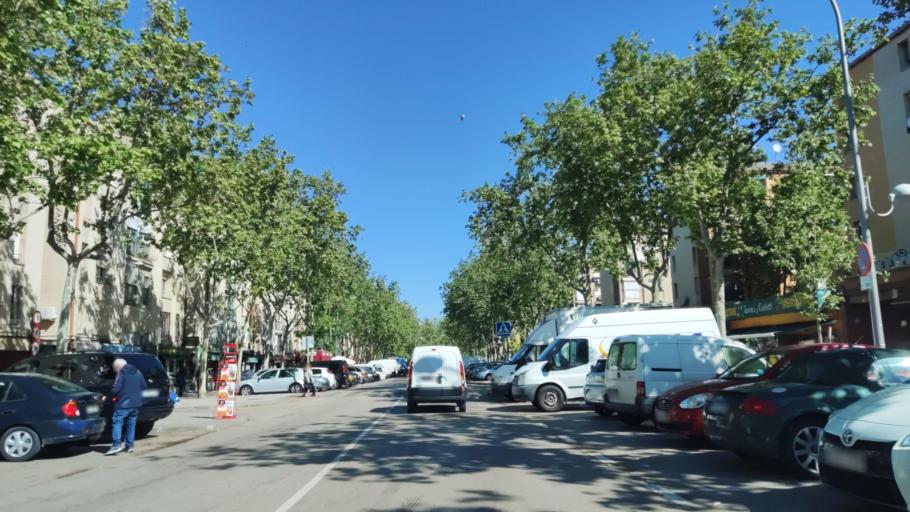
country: ES
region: Madrid
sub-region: Provincia de Madrid
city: San Blas
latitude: 40.4264
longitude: -3.6215
